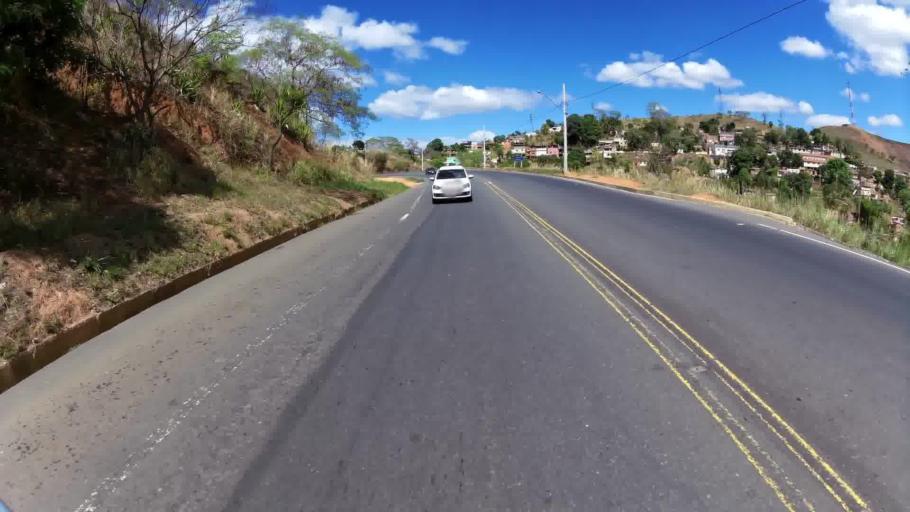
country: BR
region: Minas Gerais
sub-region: Alem Paraiba
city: Alem Paraiba
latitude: -21.8630
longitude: -42.6720
